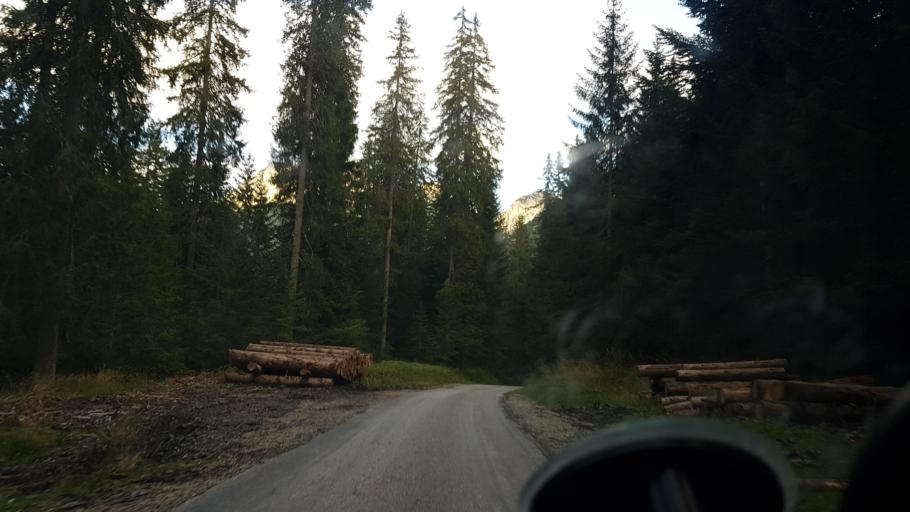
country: IT
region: Veneto
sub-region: Provincia di Belluno
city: San Pietro di Cadore
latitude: 46.6090
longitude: 12.5992
